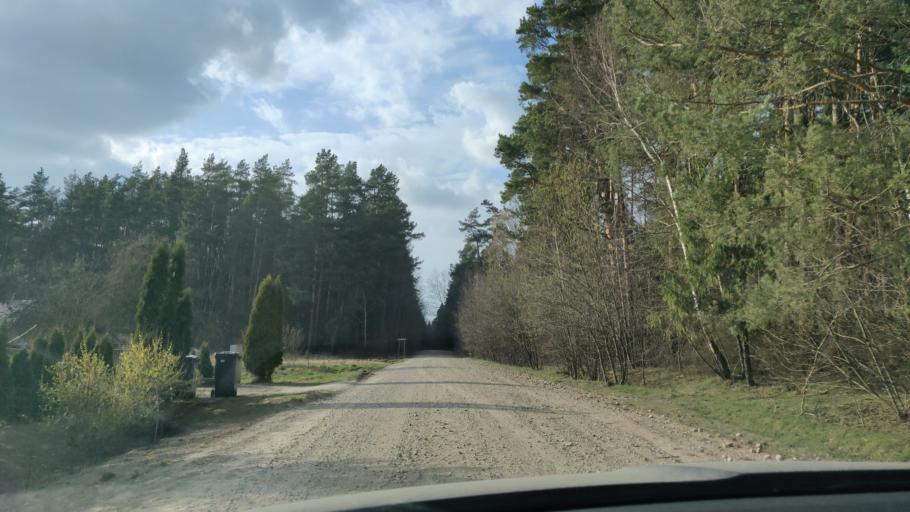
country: LT
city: Lentvaris
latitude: 54.5972
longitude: 25.0814
